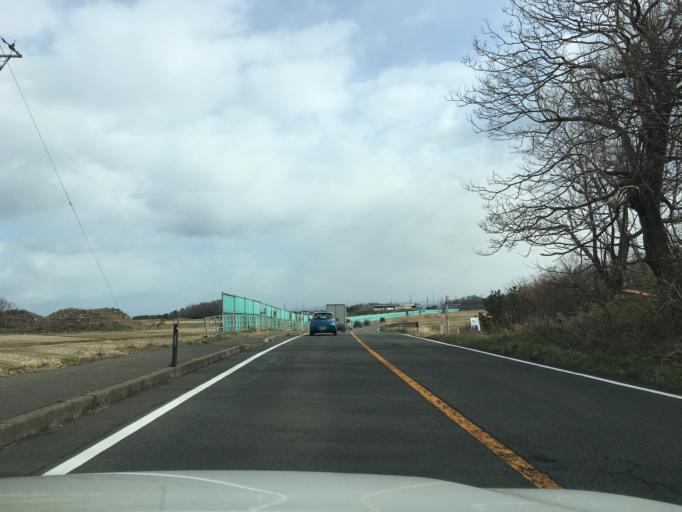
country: JP
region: Yamagata
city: Yuza
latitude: 39.2749
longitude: 139.9249
